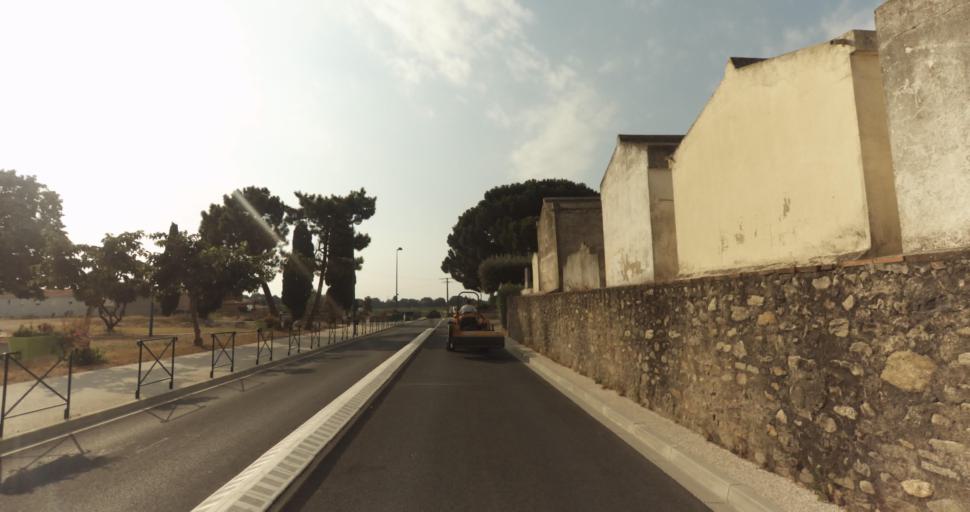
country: FR
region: Languedoc-Roussillon
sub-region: Departement des Pyrenees-Orientales
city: Corneilla-del-Vercol
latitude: 42.6248
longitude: 2.9540
